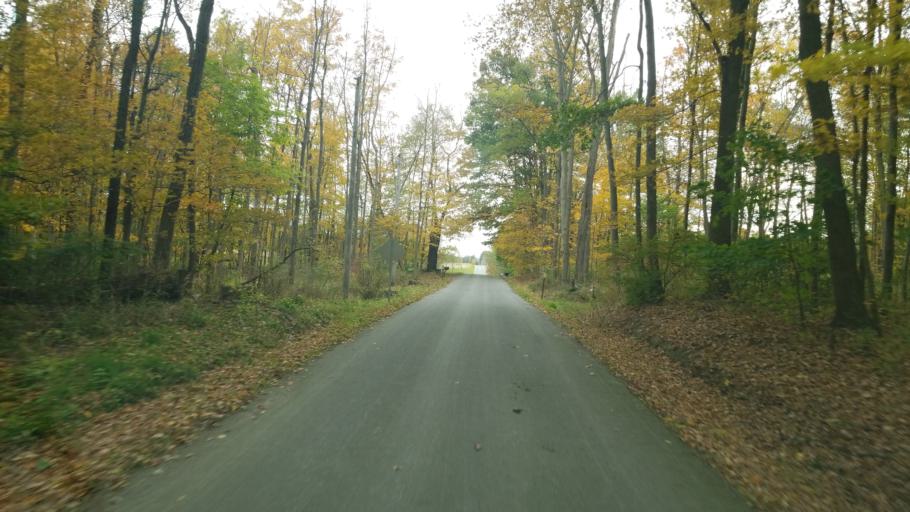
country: US
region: Ohio
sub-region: Ashland County
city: Ashland
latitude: 40.8948
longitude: -82.2398
